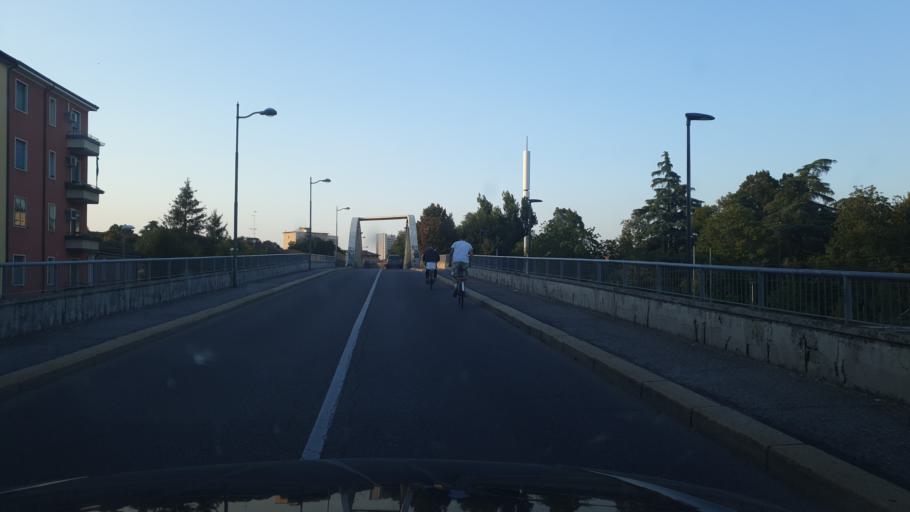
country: IT
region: Emilia-Romagna
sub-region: Provincia di Bologna
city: Bologna
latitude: 44.4984
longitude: 11.3656
